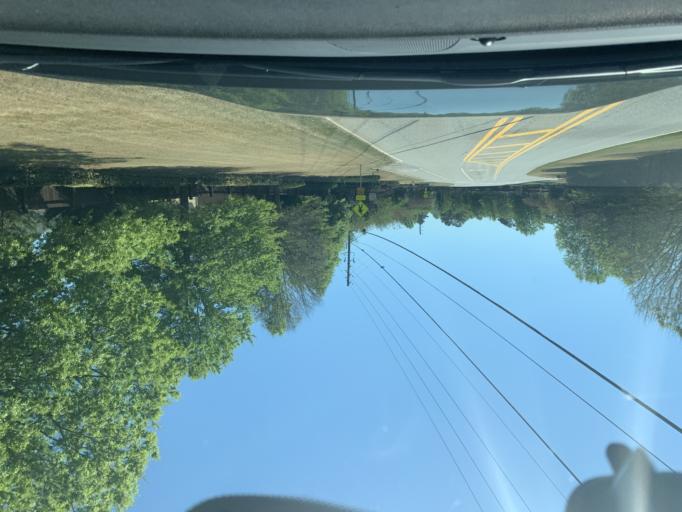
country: US
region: Georgia
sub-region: Forsyth County
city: Cumming
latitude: 34.1779
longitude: -84.1687
